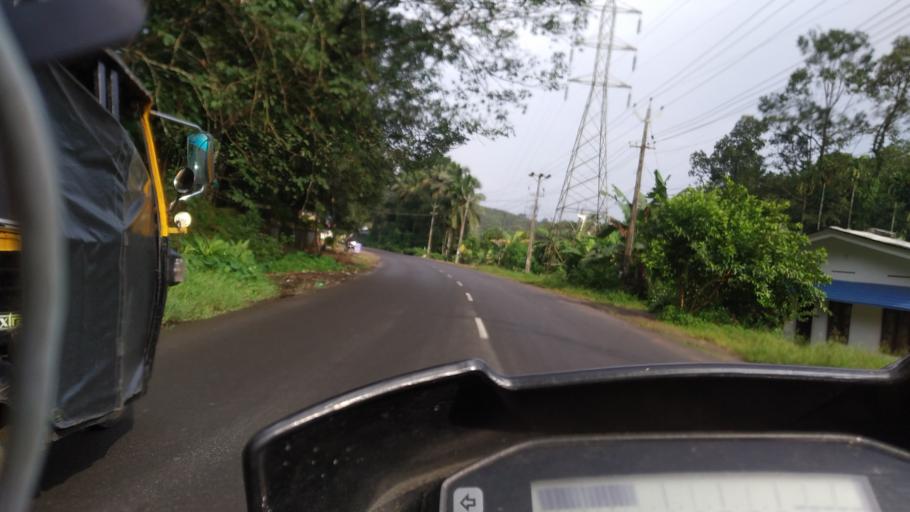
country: IN
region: Kerala
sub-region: Ernakulam
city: Kotamangalam
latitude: 10.0525
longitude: 76.7030
